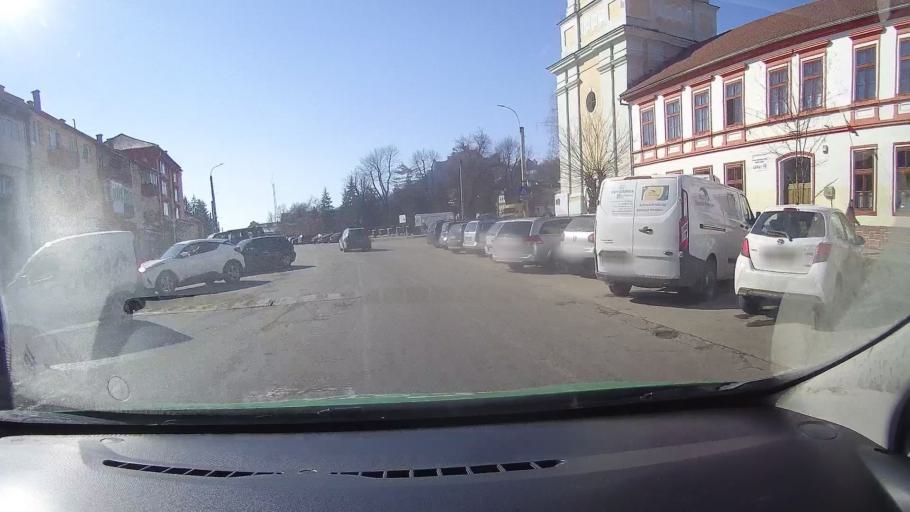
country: RO
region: Brasov
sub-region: Oras Rupea
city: Rupea
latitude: 46.0389
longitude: 25.2221
